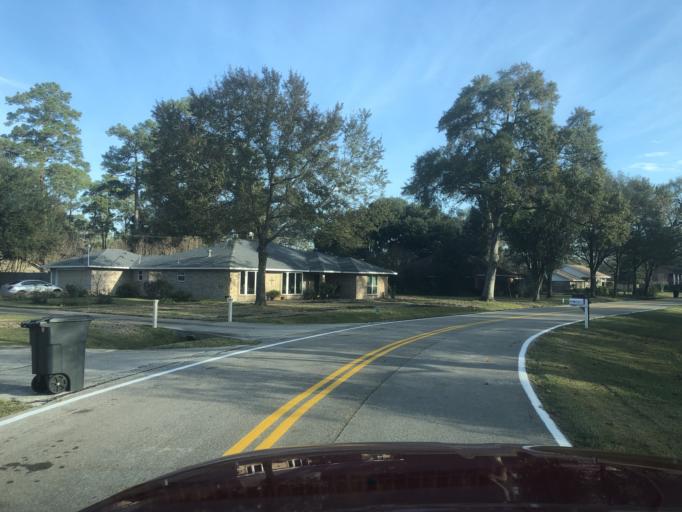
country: US
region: Texas
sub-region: Harris County
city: Spring
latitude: 30.0154
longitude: -95.4738
